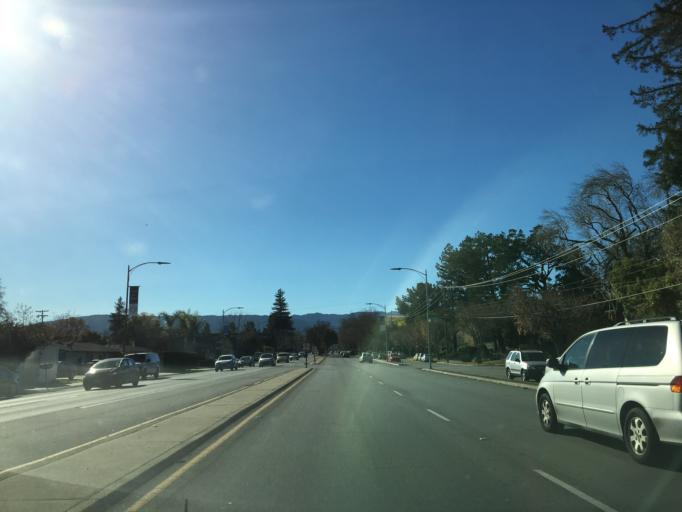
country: US
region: California
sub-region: Santa Clara County
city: Campbell
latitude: 37.2981
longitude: -121.9848
